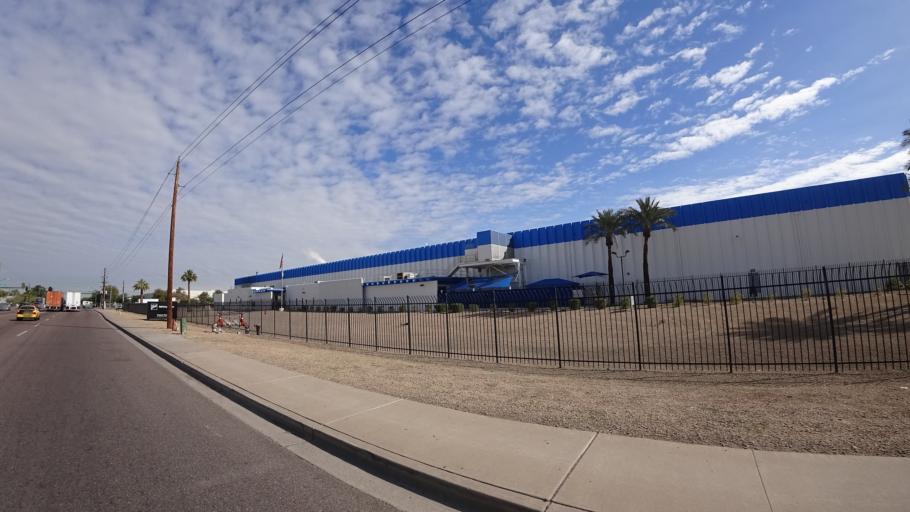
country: US
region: Arizona
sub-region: Maricopa County
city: Laveen
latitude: 33.4496
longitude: -112.1691
